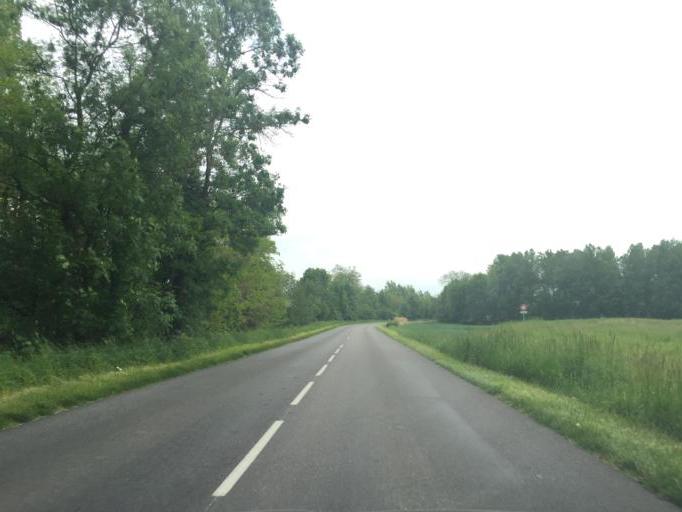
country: FR
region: Rhone-Alpes
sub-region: Departement de la Drome
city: Peyrins
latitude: 45.0756
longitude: 5.0405
